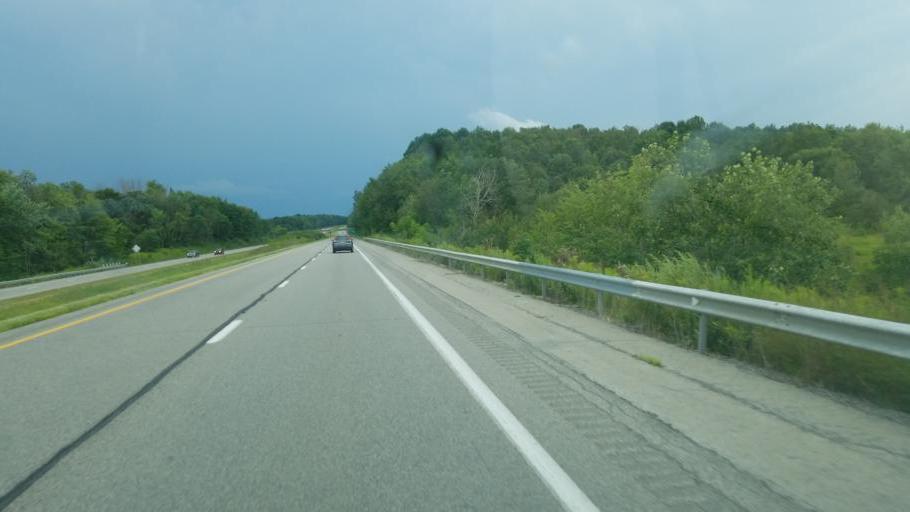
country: US
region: Pennsylvania
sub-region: Mercer County
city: Stoneboro
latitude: 41.3020
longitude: -80.1582
